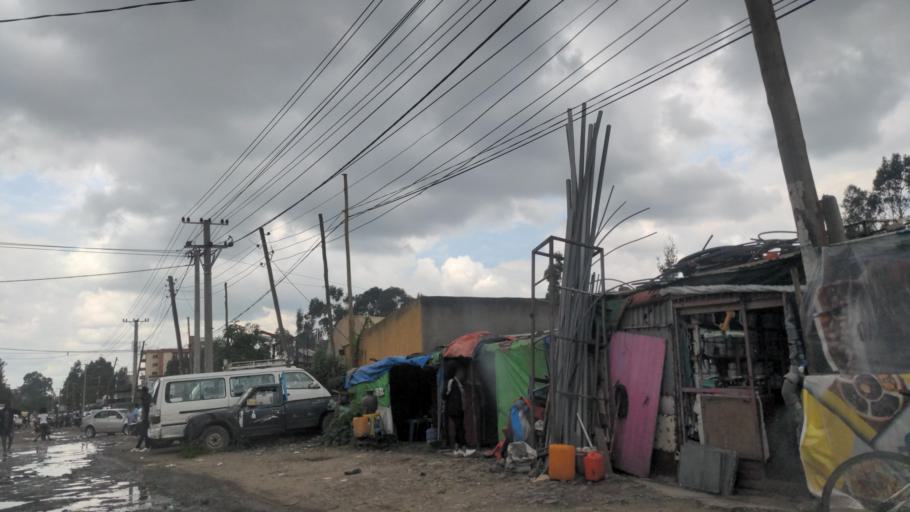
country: ET
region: Adis Abeba
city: Addis Ababa
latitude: 9.0147
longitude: 38.7908
